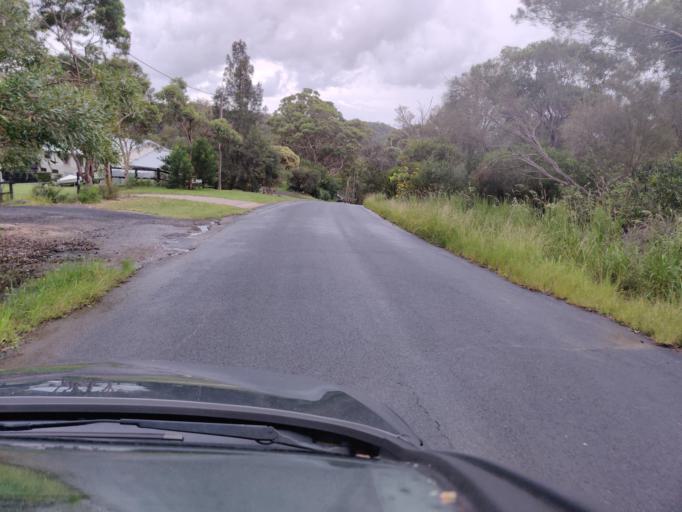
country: AU
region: New South Wales
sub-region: Pittwater
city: Ingleside
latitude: -33.6780
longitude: 151.2535
